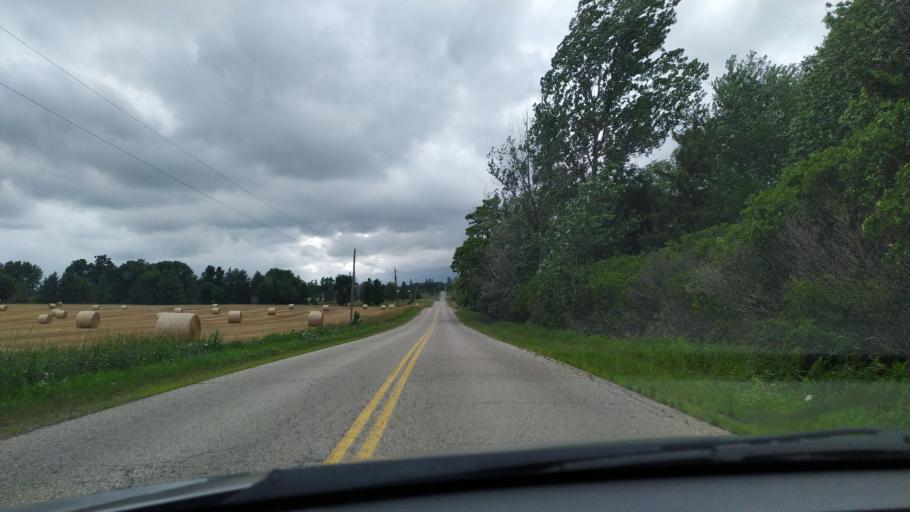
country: CA
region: Ontario
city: Kitchener
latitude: 43.3373
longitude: -80.6150
